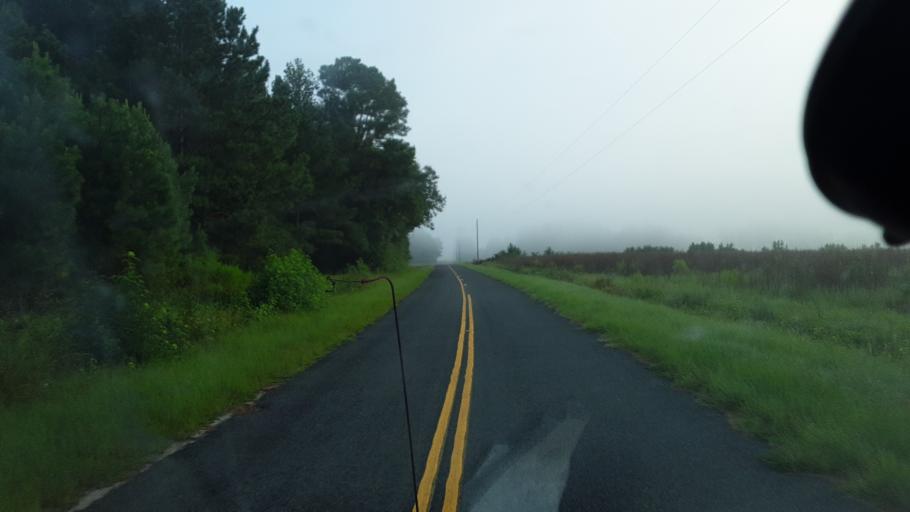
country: US
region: South Carolina
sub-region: Williamsburg County
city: Kingstree
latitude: 33.7997
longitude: -79.9644
